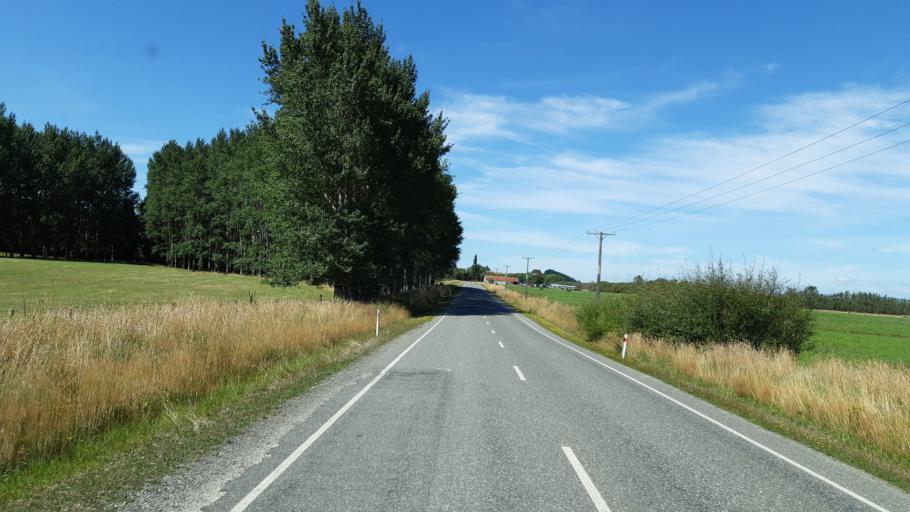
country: NZ
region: Southland
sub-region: Gore District
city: Gore
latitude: -46.0041
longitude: 168.8799
